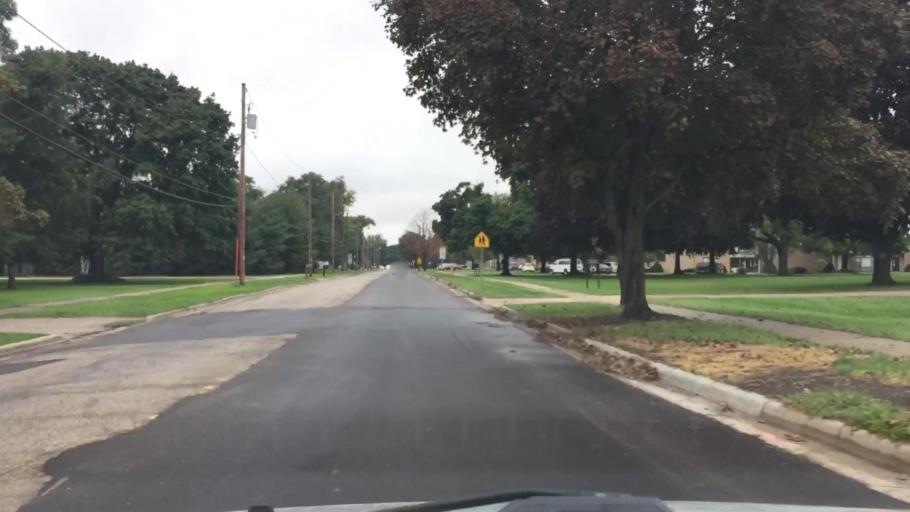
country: US
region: Wisconsin
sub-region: Rock County
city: Janesville
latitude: 42.6643
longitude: -89.0361
